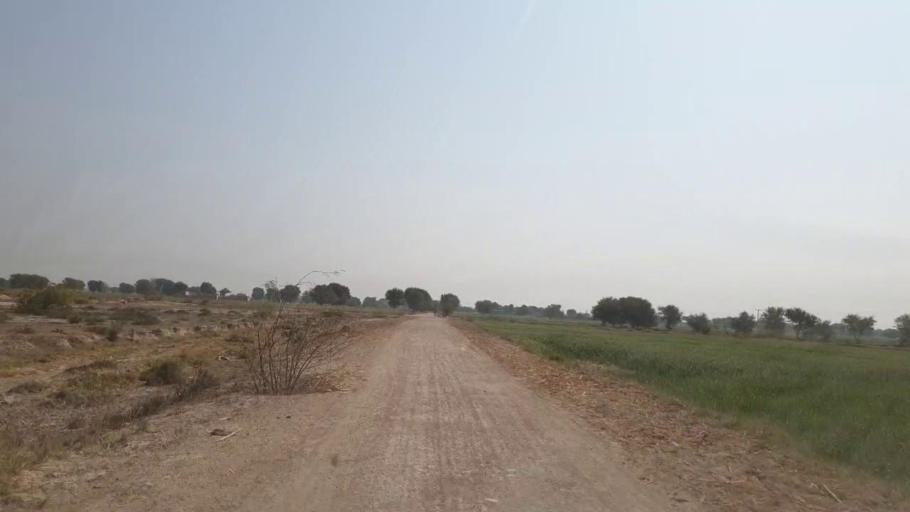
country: PK
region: Sindh
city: Mirpur Khas
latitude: 25.6487
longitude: 69.1140
